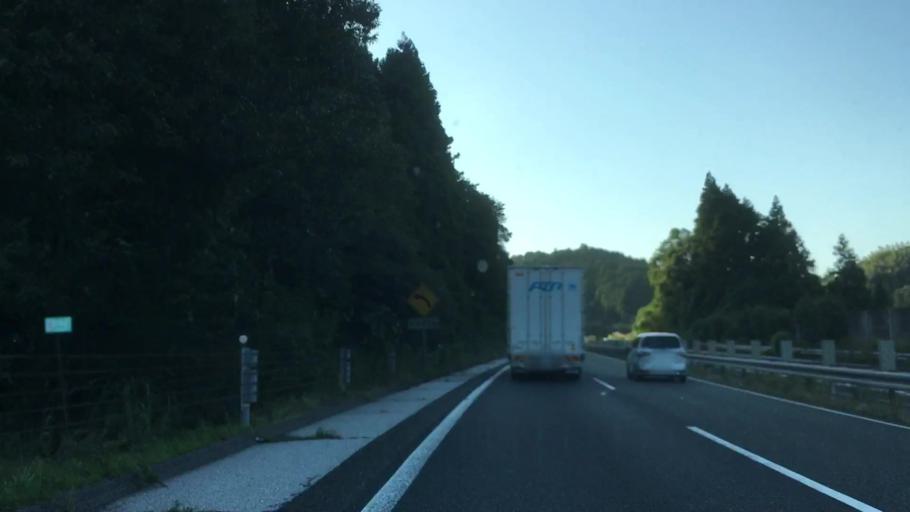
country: JP
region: Yamaguchi
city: Onoda
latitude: 34.1158
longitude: 131.1279
